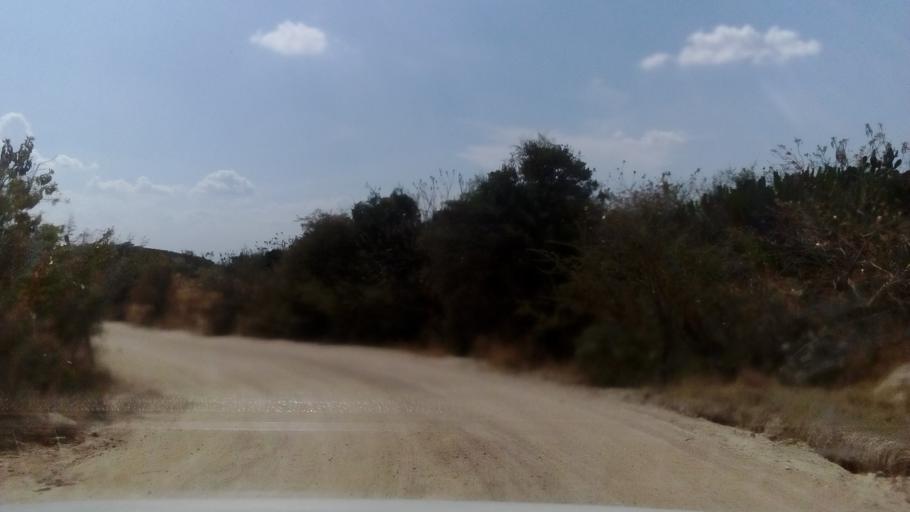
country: MX
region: Guanajuato
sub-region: Silao de la Victoria
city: Loma de Yerbabuena
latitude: 21.0850
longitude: -101.4460
